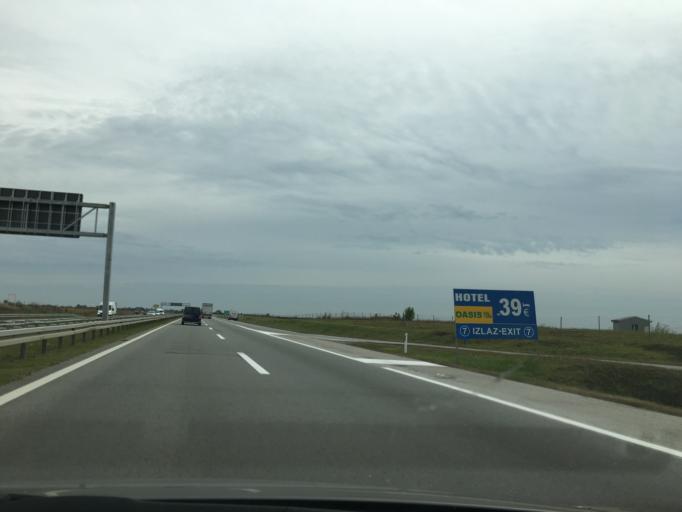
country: RS
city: Novi Banovci
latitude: 44.9424
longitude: 20.2834
